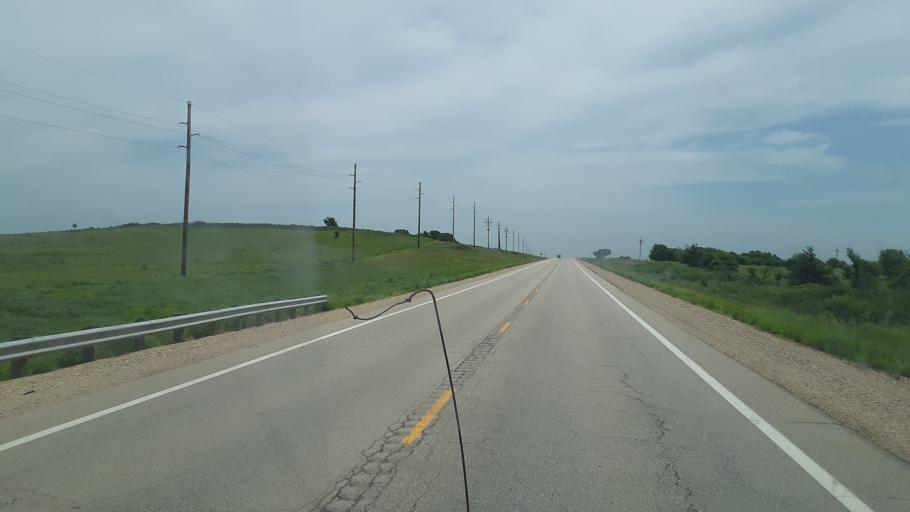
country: US
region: Kansas
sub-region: Greenwood County
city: Eureka
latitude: 37.8372
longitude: -96.0549
